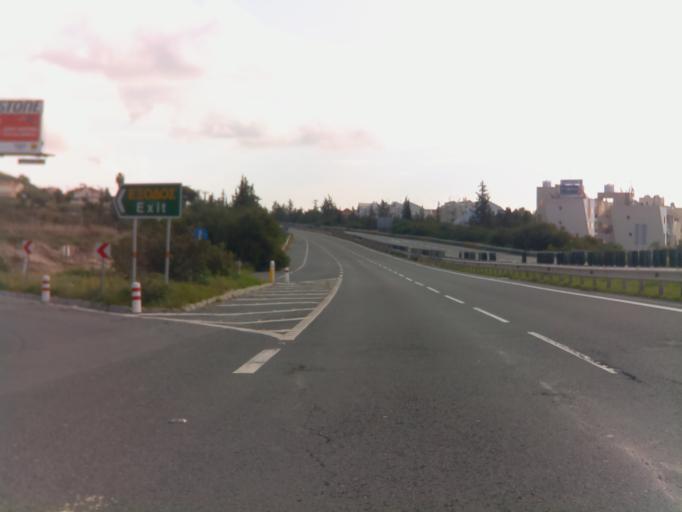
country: CY
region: Larnaka
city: Agios Tychon
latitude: 34.7161
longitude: 33.1619
